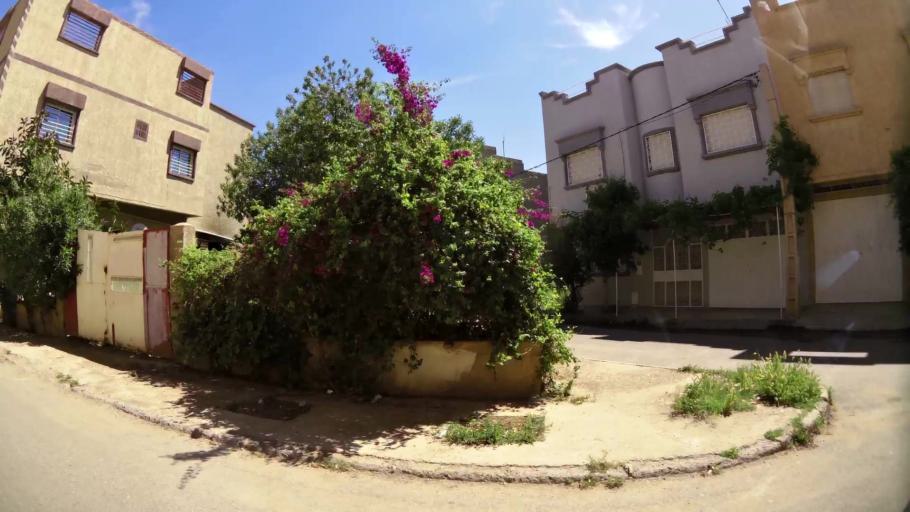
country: MA
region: Oriental
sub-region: Oujda-Angad
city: Oujda
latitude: 34.6602
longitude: -1.9329
